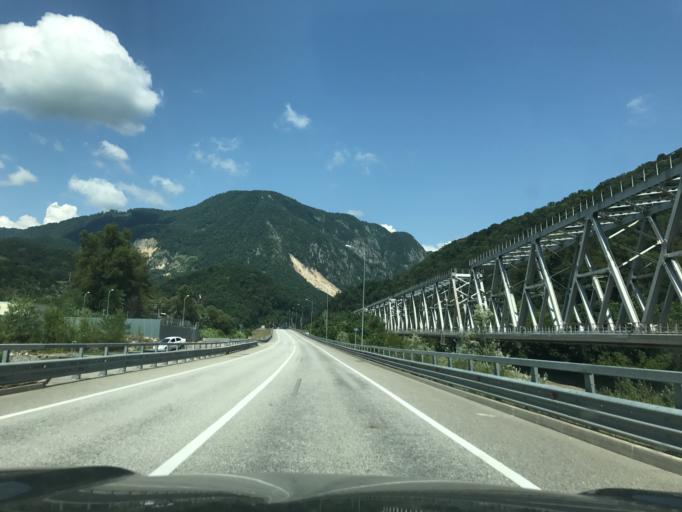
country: RU
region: Krasnodarskiy
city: Vysokoye
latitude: 43.5724
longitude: 40.0070
